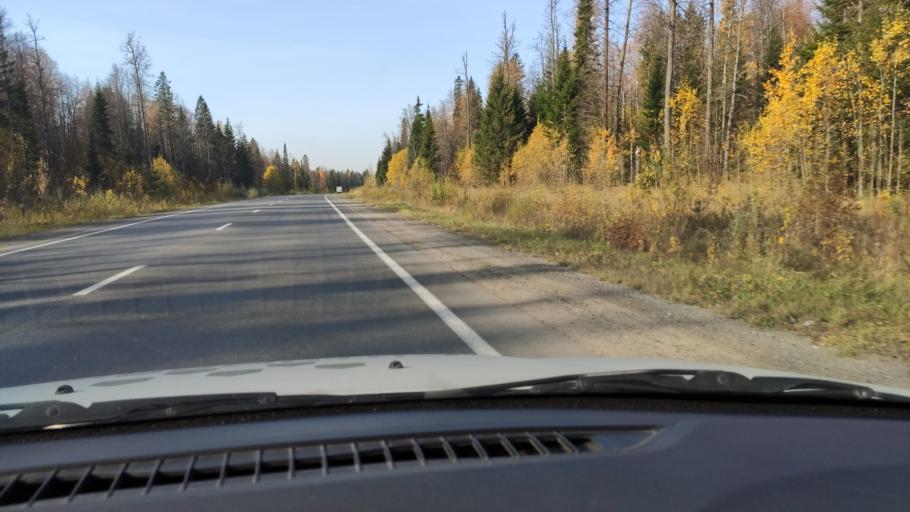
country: RU
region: Perm
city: Novyye Lyady
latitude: 58.0310
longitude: 56.4861
